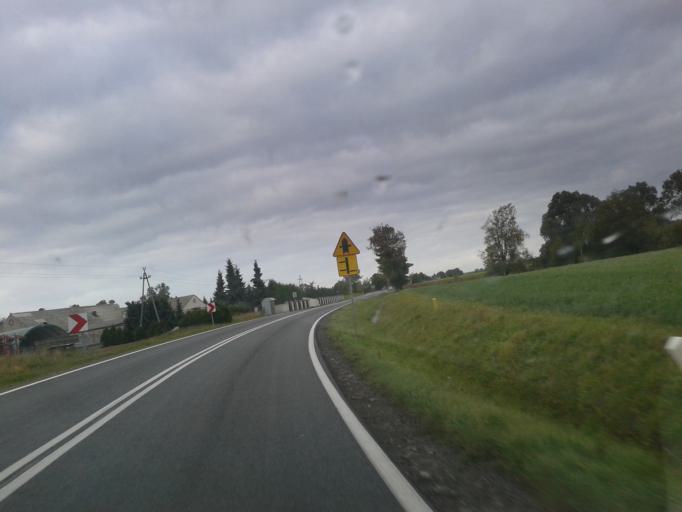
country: PL
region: Kujawsko-Pomorskie
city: Kamien Krajenski
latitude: 53.5005
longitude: 17.5071
